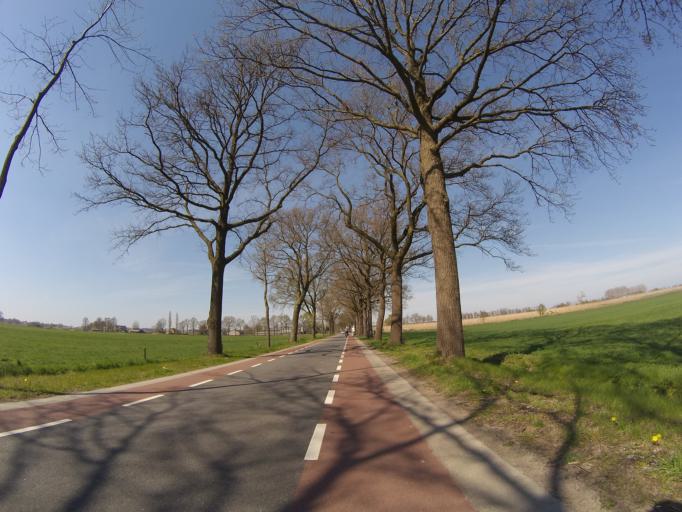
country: NL
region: Utrecht
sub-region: Gemeente Veenendaal
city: Veenendaal
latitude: 52.0055
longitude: 5.6059
